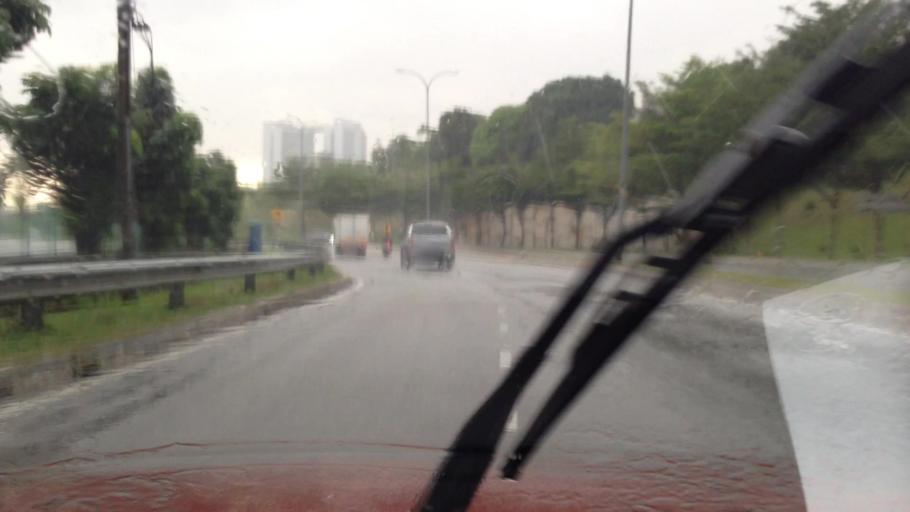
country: MY
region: Selangor
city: Subang Jaya
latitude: 3.0254
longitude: 101.5884
